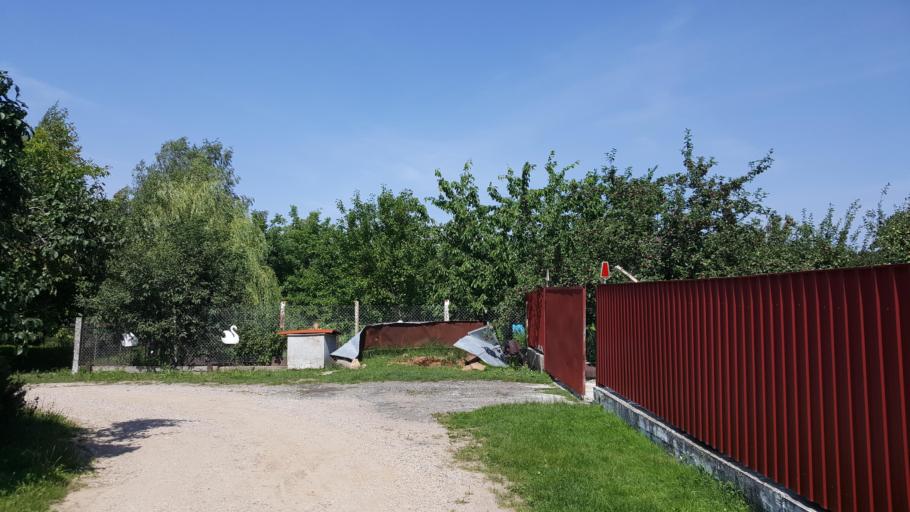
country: BY
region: Brest
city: Vysokaye
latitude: 52.3607
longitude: 23.3853
